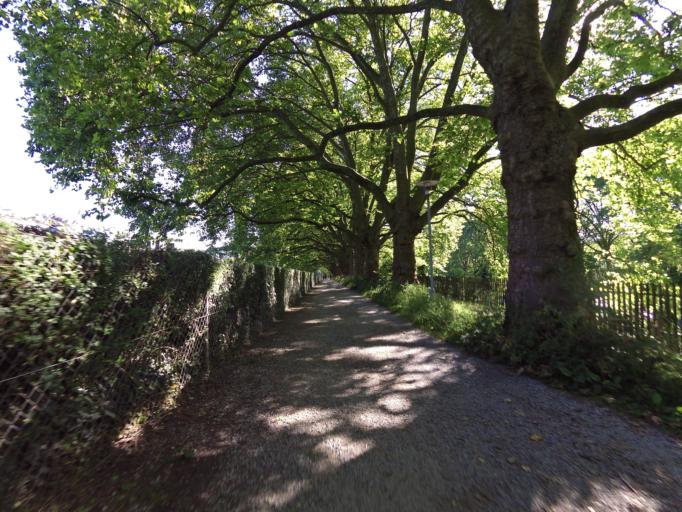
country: CH
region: Zurich
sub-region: Bezirk Zuerich
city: Zuerich (Kreis 4) / Werd
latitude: 47.3684
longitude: 8.5280
